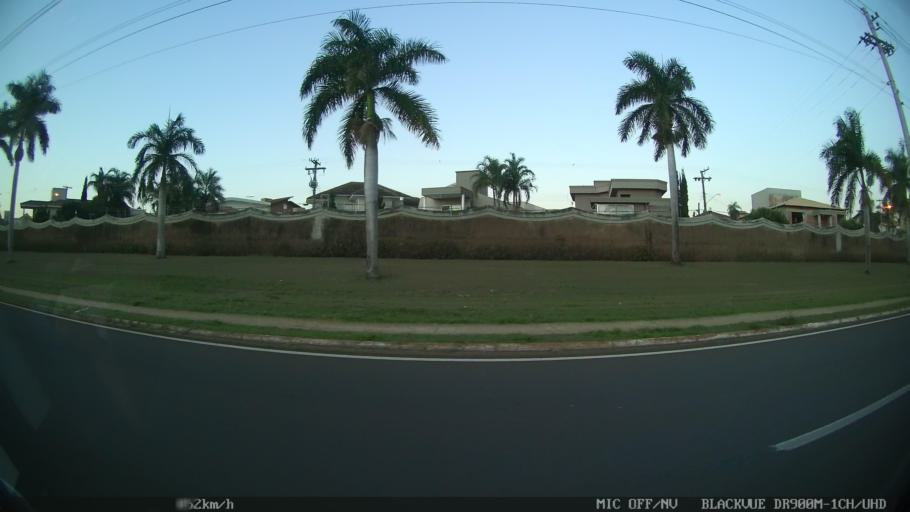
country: BR
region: Sao Paulo
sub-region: Sao Jose Do Rio Preto
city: Sao Jose do Rio Preto
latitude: -20.8158
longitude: -49.3471
